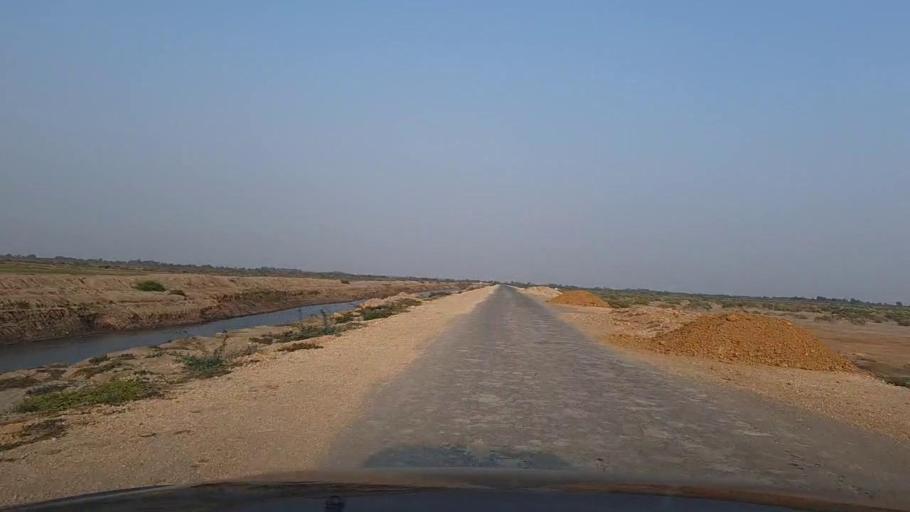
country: PK
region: Sindh
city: Mirpur Sakro
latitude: 24.4406
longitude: 67.7777
